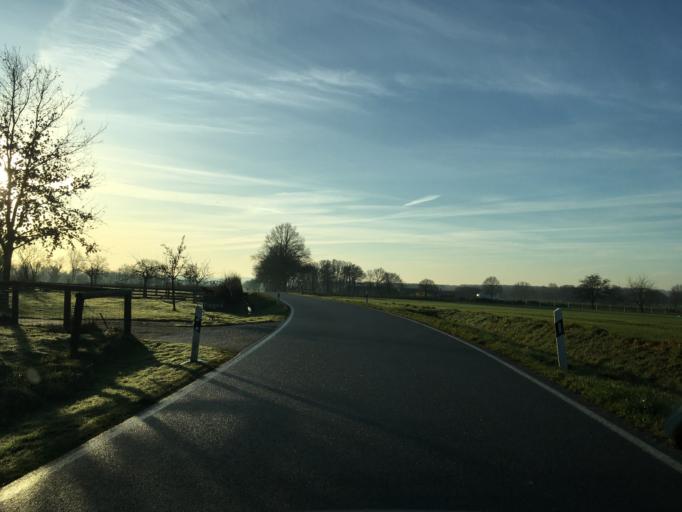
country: DE
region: North Rhine-Westphalia
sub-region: Regierungsbezirk Munster
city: Schoppingen
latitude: 52.0706
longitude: 7.2605
